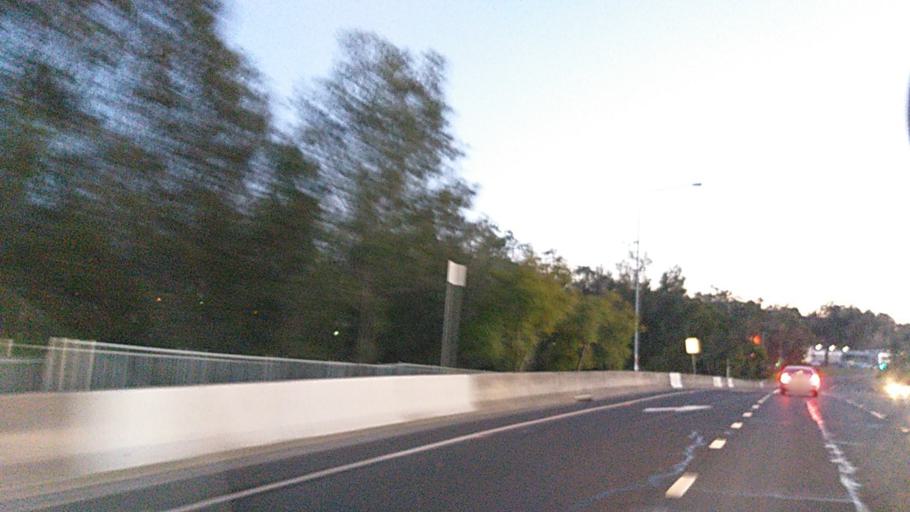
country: AU
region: New South Wales
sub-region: Campbelltown Municipality
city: Leumeah
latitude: -34.0558
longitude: 150.8239
